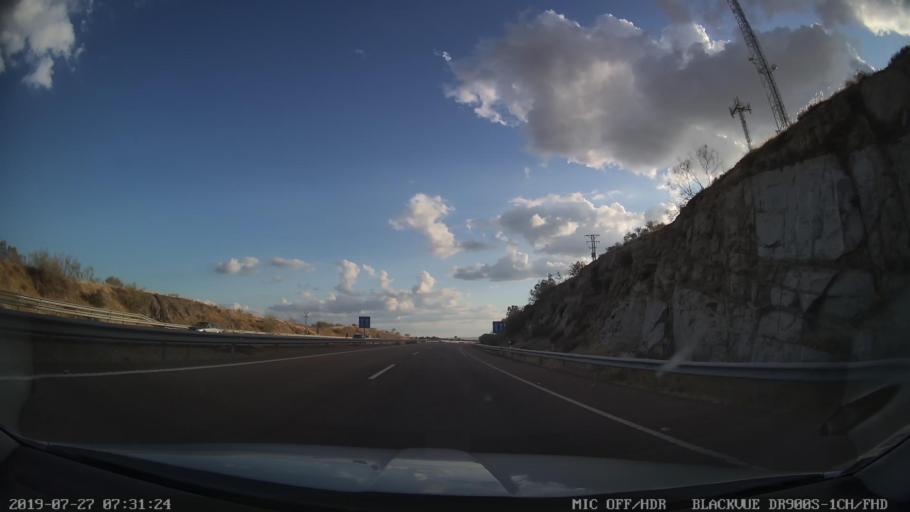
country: ES
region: Extremadura
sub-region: Provincia de Caceres
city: Escurial
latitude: 39.1716
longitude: -5.9005
